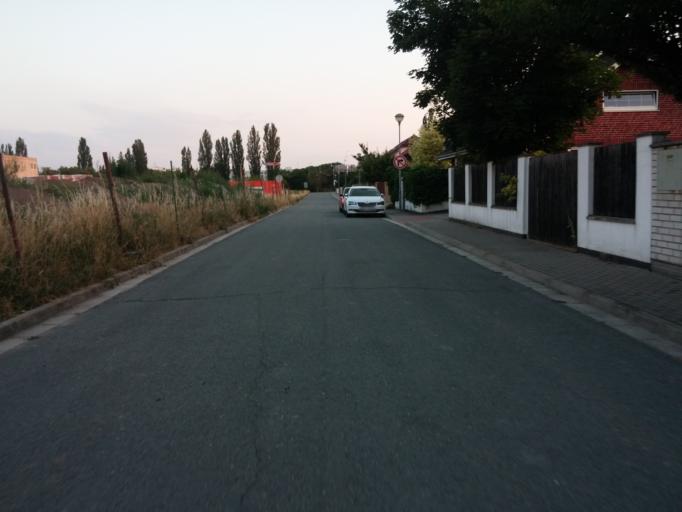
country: CZ
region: Central Bohemia
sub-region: Okres Nymburk
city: Podebrady
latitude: 50.1534
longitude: 15.1230
